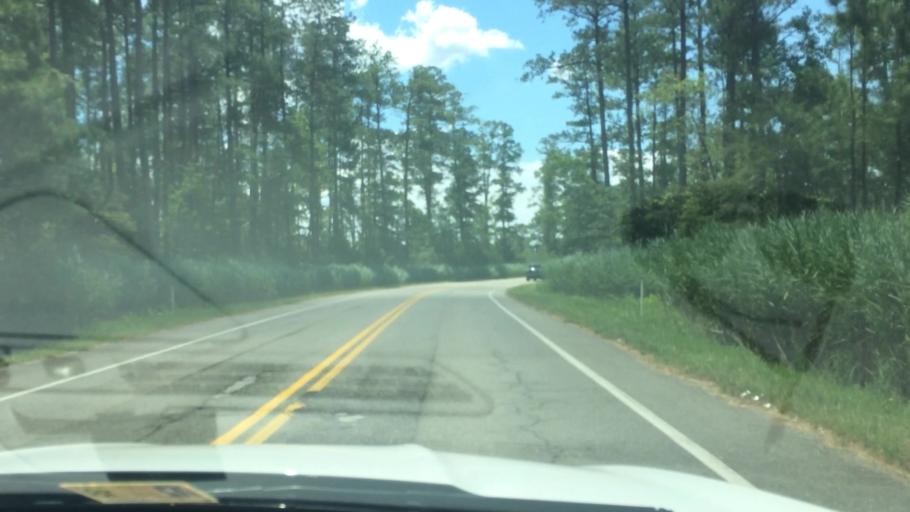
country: US
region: Virginia
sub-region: King William County
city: West Point
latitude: 37.5468
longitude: -76.7933
